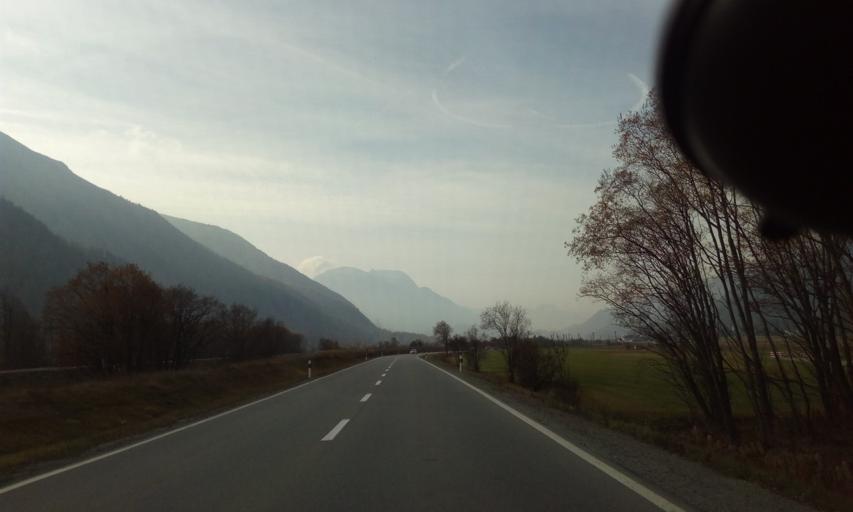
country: CH
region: Grisons
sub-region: Maloja District
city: Ponte
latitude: 46.5644
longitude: 9.9086
